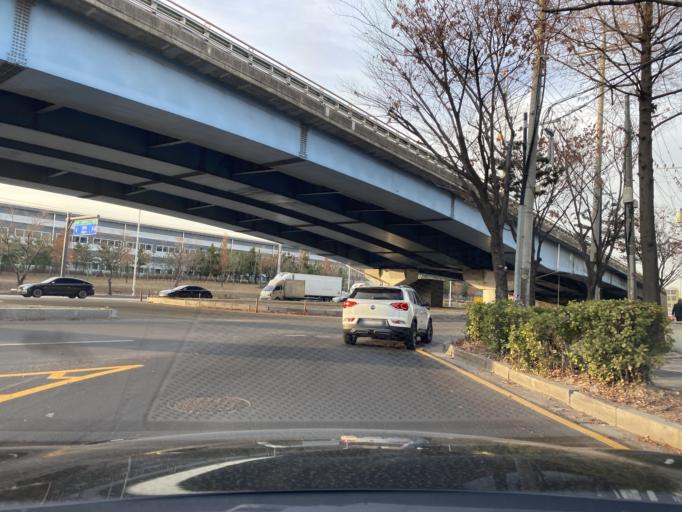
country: KR
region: Incheon
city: Incheon
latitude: 37.4995
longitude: 126.6482
